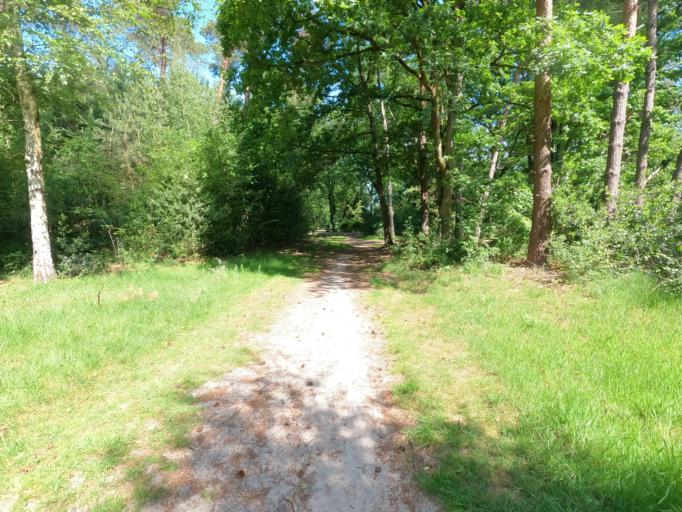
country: BE
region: Flanders
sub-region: Provincie Antwerpen
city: Kalmthout
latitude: 51.3680
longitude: 4.4894
